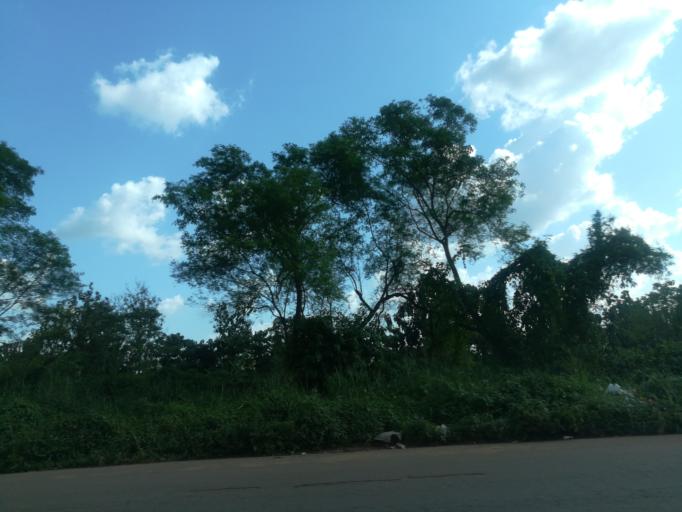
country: NG
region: Oyo
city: Egbeda
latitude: 7.4236
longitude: 3.9825
